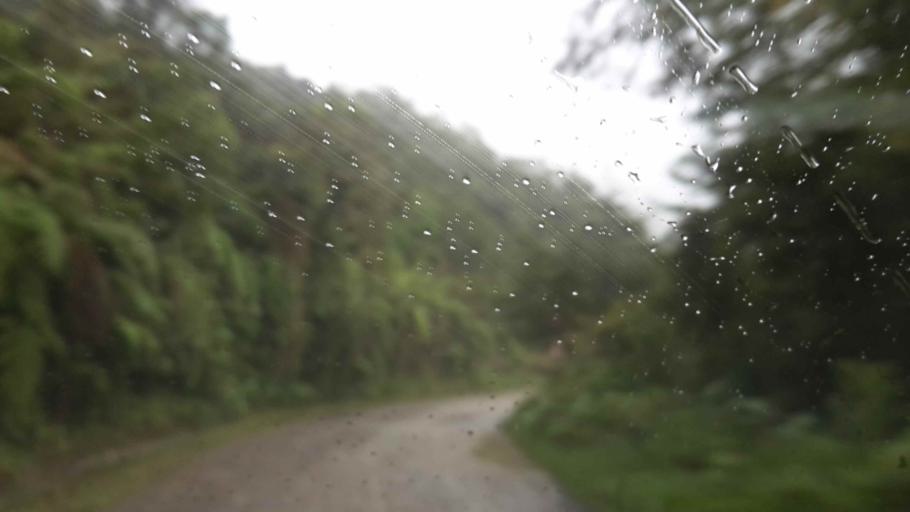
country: BO
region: Cochabamba
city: Colomi
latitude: -17.1551
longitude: -65.9091
